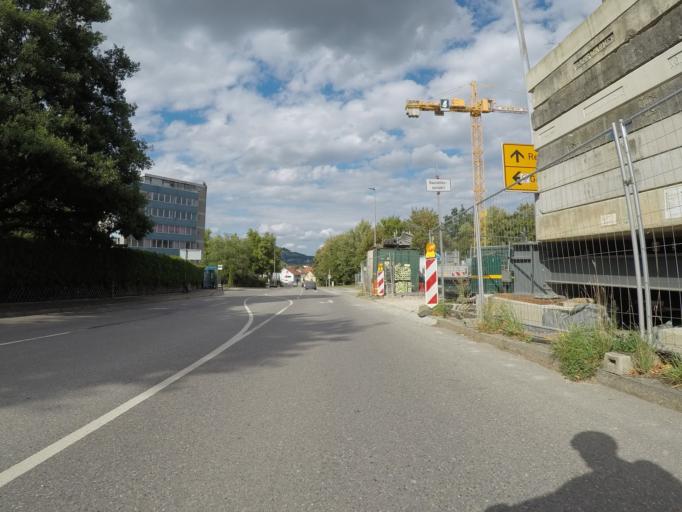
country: DE
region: Baden-Wuerttemberg
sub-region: Tuebingen Region
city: Pfullingen
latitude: 48.4559
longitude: 9.2189
